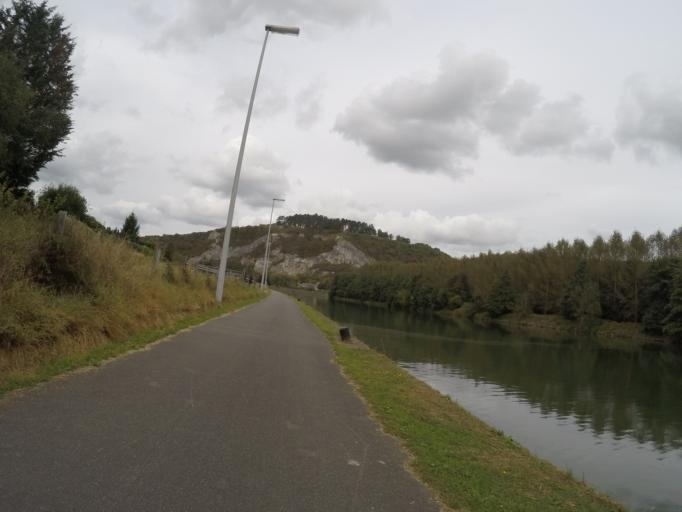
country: BE
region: Wallonia
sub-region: Province de Namur
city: Anhee
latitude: 50.2987
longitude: 4.8957
